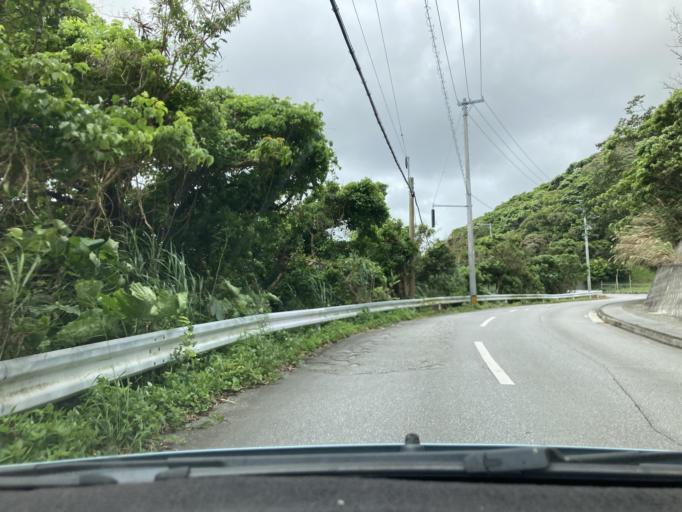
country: JP
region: Okinawa
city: Ginowan
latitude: 26.2302
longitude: 127.7473
